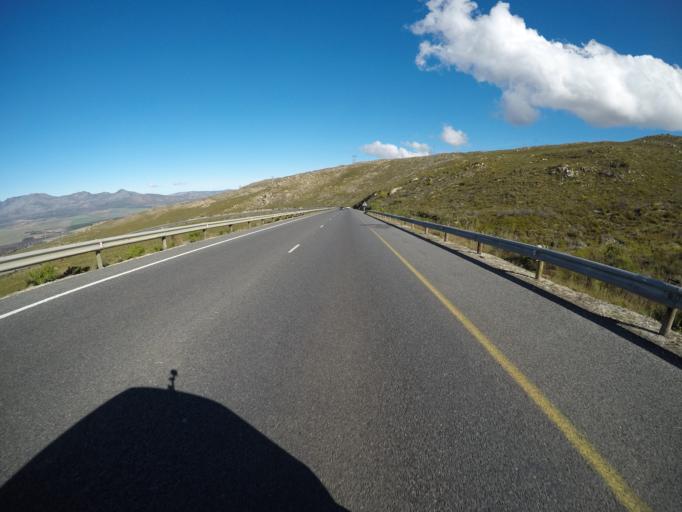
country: ZA
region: Western Cape
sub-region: Overberg District Municipality
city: Grabouw
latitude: -34.2207
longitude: 19.1729
